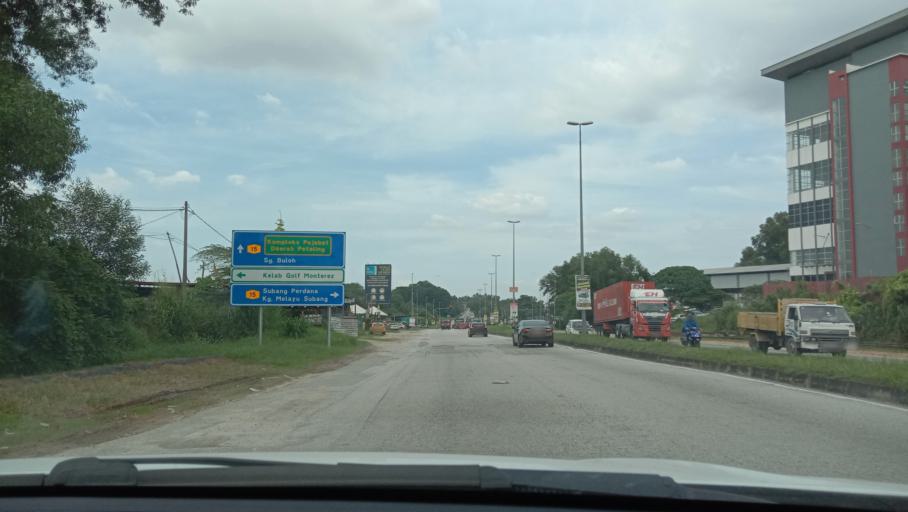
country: MY
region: Selangor
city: Kampung Baru Subang
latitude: 3.1355
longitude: 101.5258
